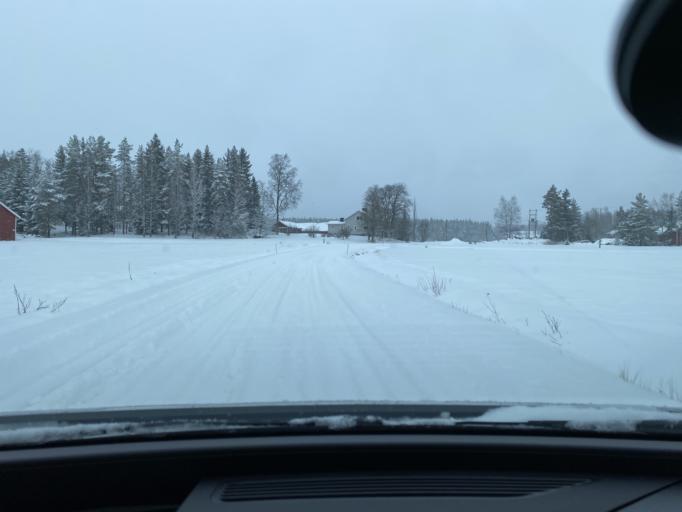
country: FI
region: Haeme
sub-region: Forssa
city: Humppila
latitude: 61.0116
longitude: 23.3032
